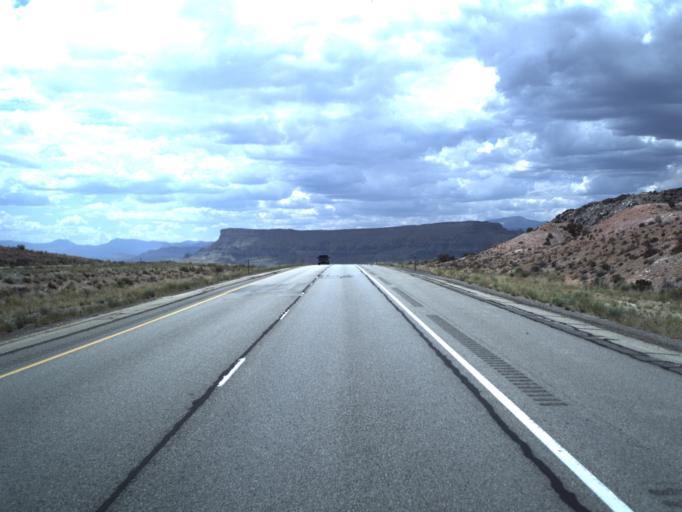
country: US
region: Utah
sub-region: Emery County
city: Ferron
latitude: 38.8238
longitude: -111.1472
